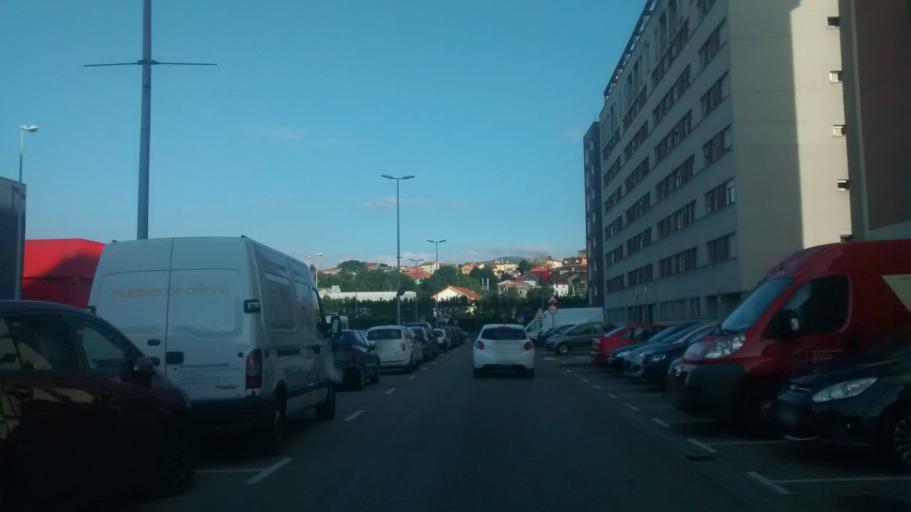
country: ES
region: Cantabria
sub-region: Provincia de Cantabria
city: El Astillero
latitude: 43.4231
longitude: -3.8404
